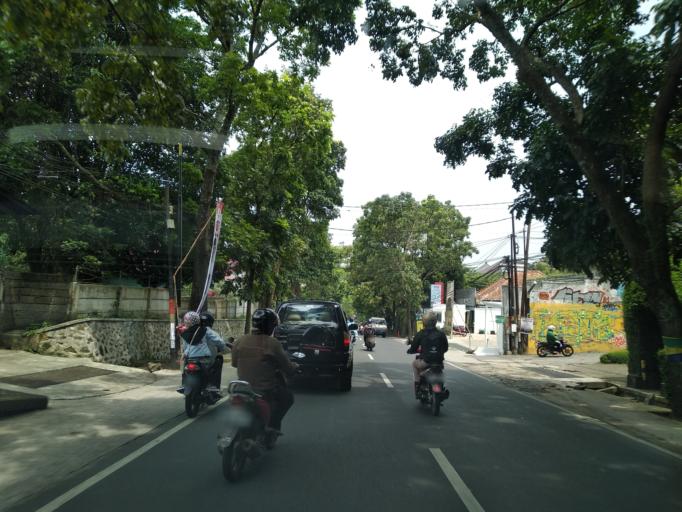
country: ID
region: West Java
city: Lembang
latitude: -6.8561
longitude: 107.5956
